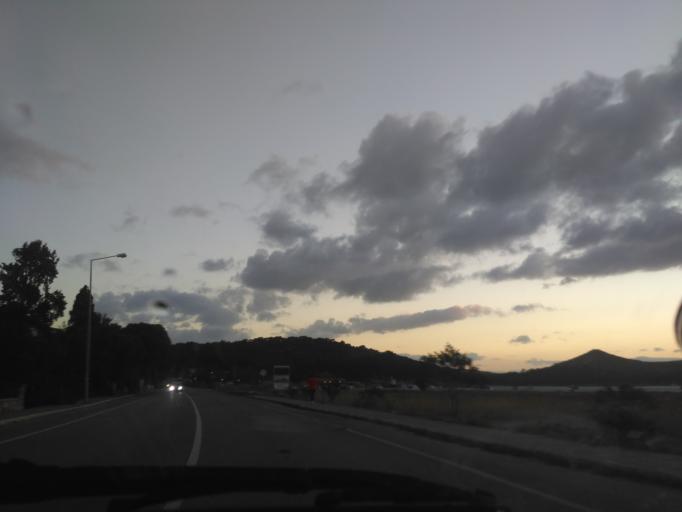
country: TR
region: Balikesir
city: Ayvalik
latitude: 39.3037
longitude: 26.6637
